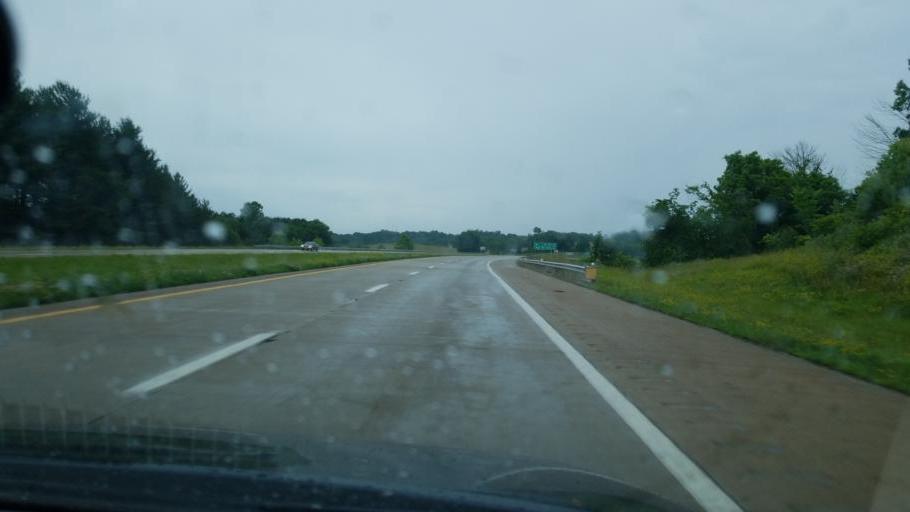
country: US
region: Ohio
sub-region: Athens County
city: Athens
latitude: 39.2515
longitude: -81.9020
